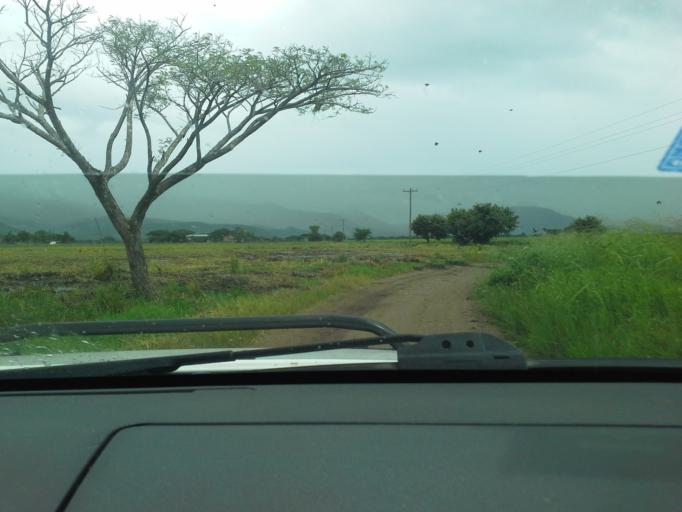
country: NI
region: Matagalpa
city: Ciudad Dario
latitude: 12.8513
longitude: -86.1789
